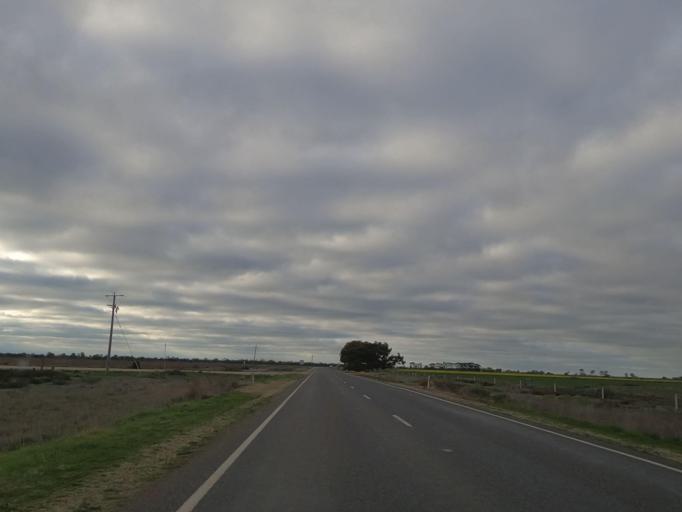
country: AU
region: Victoria
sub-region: Swan Hill
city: Swan Hill
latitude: -35.8321
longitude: 143.9436
